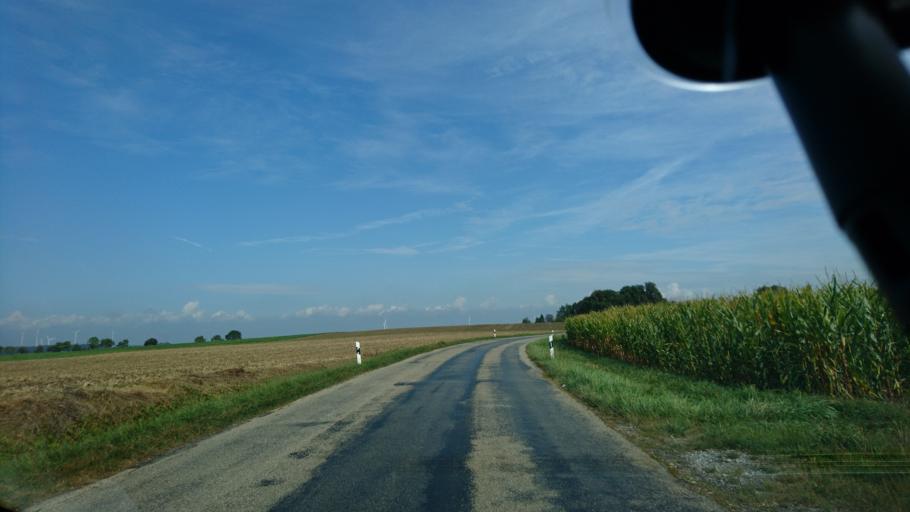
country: DE
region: Baden-Wuerttemberg
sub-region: Regierungsbezirk Stuttgart
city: Ilshofen
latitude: 49.1477
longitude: 9.9250
